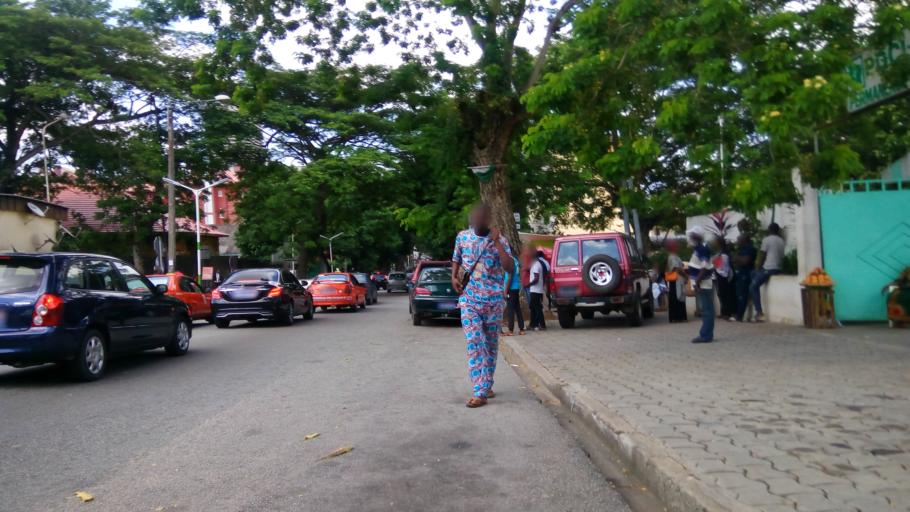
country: CI
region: Lagunes
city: Abidjan
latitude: 5.3300
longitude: -4.0217
